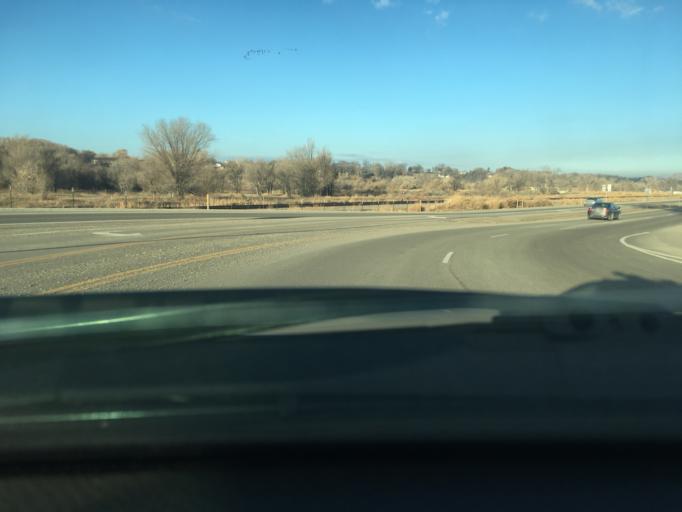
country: US
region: Colorado
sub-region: Delta County
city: Delta
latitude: 38.7306
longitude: -108.0706
